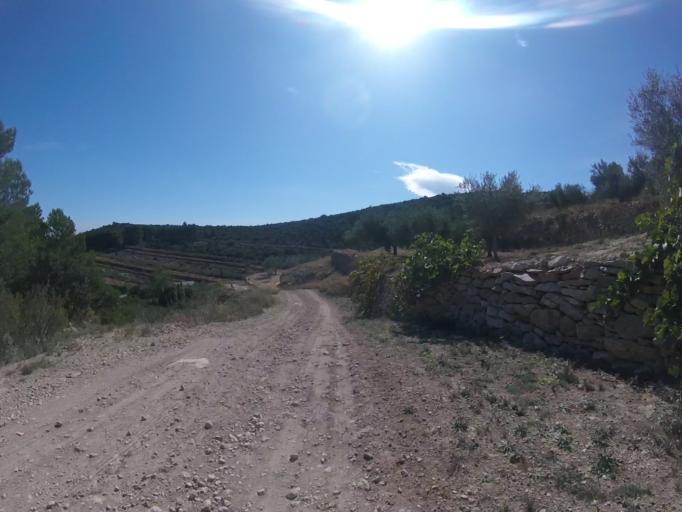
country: ES
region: Valencia
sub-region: Provincia de Castello
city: Sierra-Engarceran
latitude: 40.2711
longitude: 0.0102
